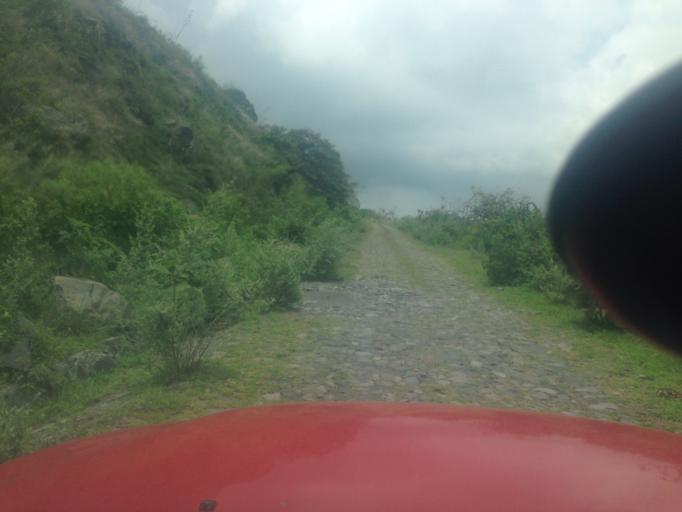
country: MX
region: Nayarit
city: Jala
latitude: 21.1212
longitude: -104.5004
